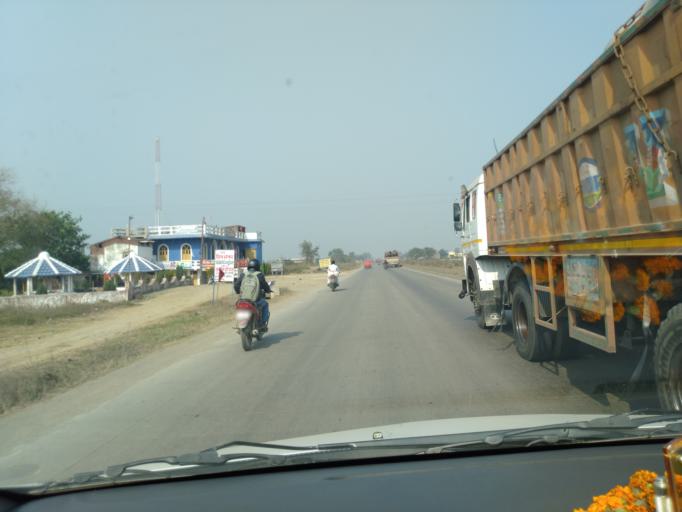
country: IN
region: Bihar
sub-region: Aurangabad
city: Aurangabad
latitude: 24.8073
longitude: 84.2985
